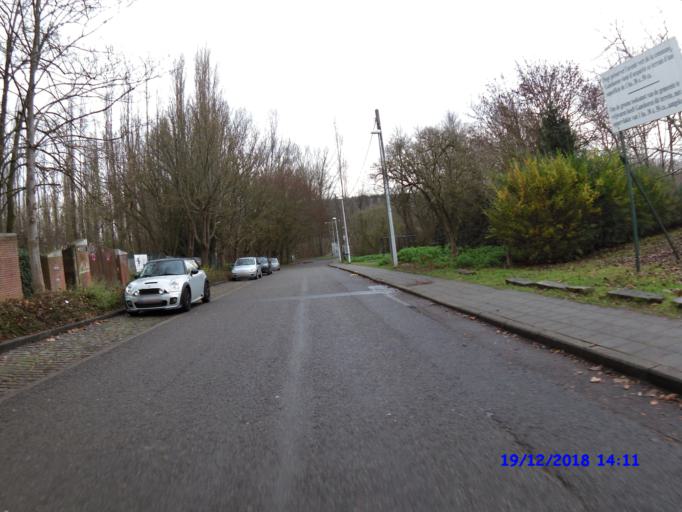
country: BE
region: Flanders
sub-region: Provincie Vlaams-Brabant
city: Wemmel
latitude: 50.8781
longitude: 4.3010
